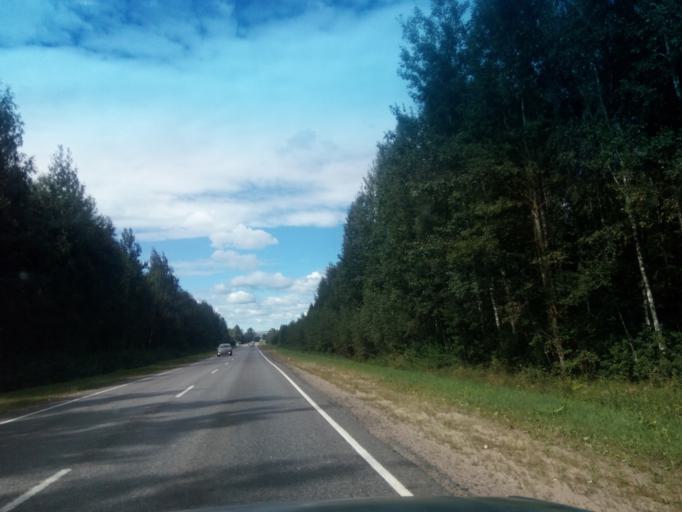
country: BY
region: Vitebsk
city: Polatsk
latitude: 55.5050
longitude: 28.7308
